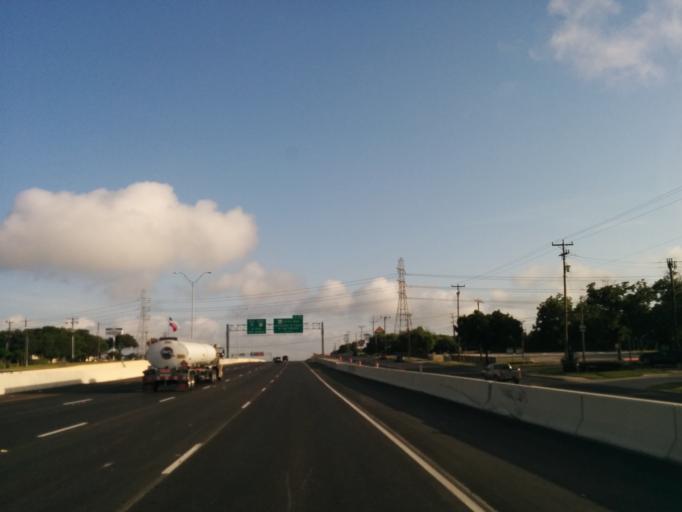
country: US
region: Texas
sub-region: Bexar County
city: Shavano Park
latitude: 29.5535
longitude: -98.5867
